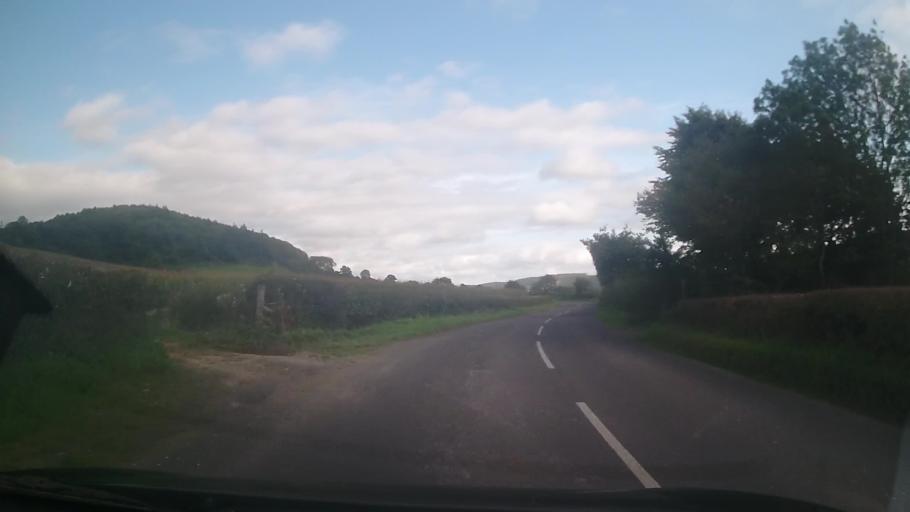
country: GB
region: England
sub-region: Shropshire
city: Bishop's Castle
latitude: 52.4688
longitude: -2.9793
